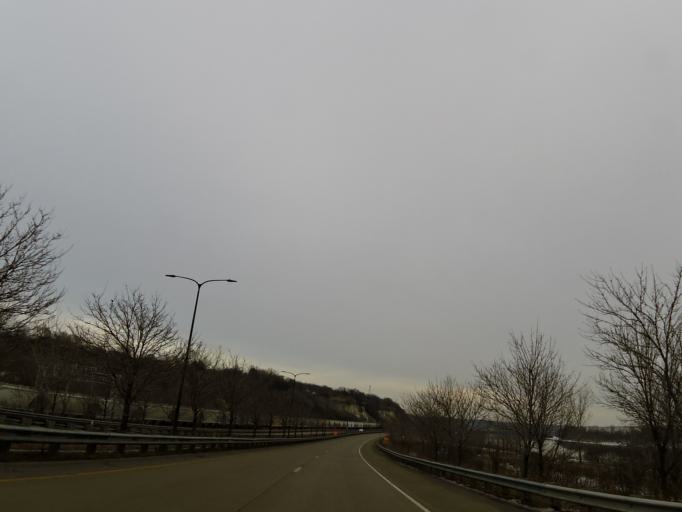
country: US
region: Minnesota
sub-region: Ramsey County
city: Saint Paul
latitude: 44.9493
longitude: -93.0735
